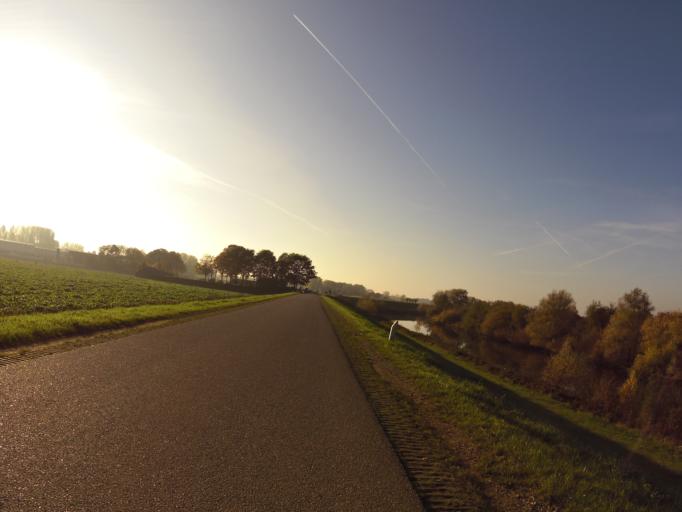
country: NL
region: Gelderland
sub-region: Gemeente Maasdriel
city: Hedel
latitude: 51.7327
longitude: 5.2664
